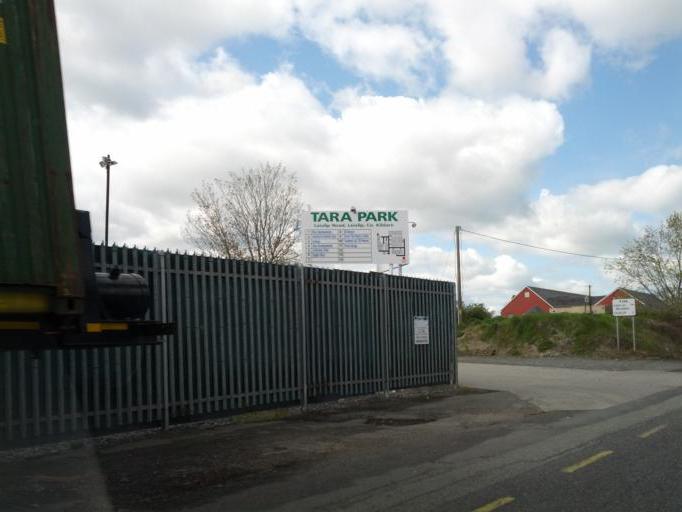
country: IE
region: Leinster
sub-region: Kildare
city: Leixlip
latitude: 53.3601
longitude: -6.4769
